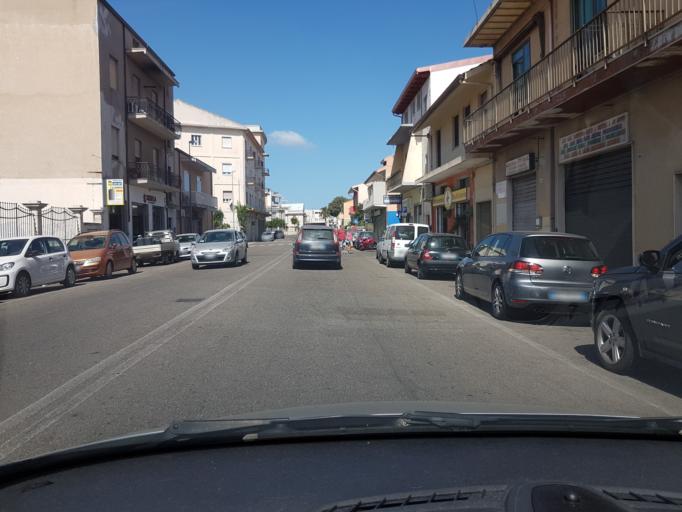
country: IT
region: Sardinia
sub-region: Provincia di Oristano
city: Oristano
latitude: 39.9079
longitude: 8.5985
